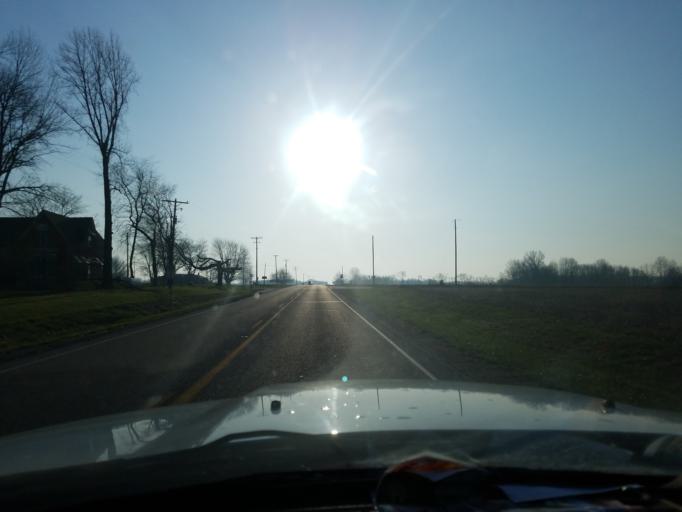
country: US
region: Indiana
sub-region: Vigo County
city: Seelyville
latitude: 39.3902
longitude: -87.2409
